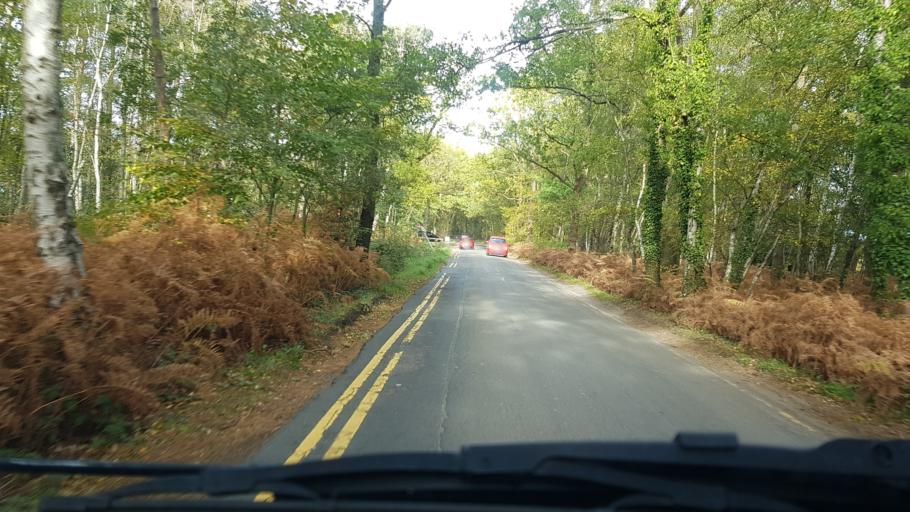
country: GB
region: England
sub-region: Surrey
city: Byfleet
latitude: 51.3143
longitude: -0.4698
